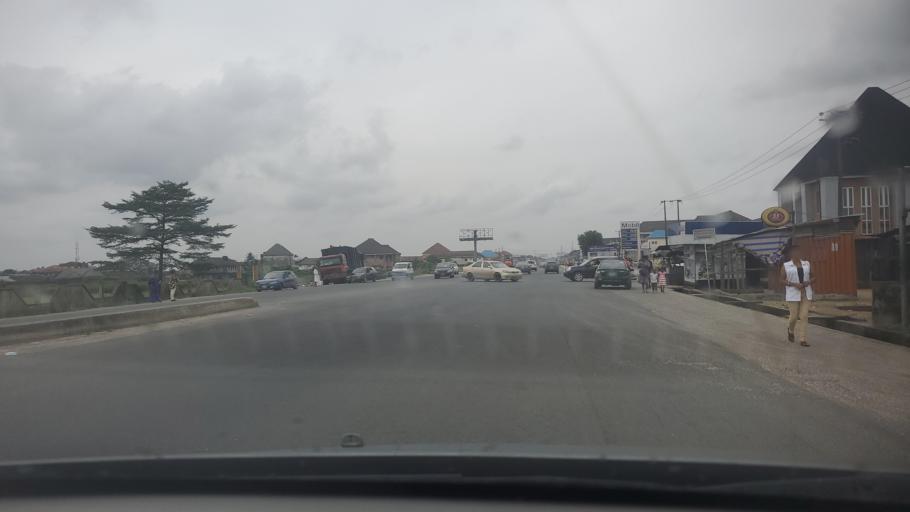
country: NG
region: Rivers
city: Port Harcourt
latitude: 4.8700
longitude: 6.9746
